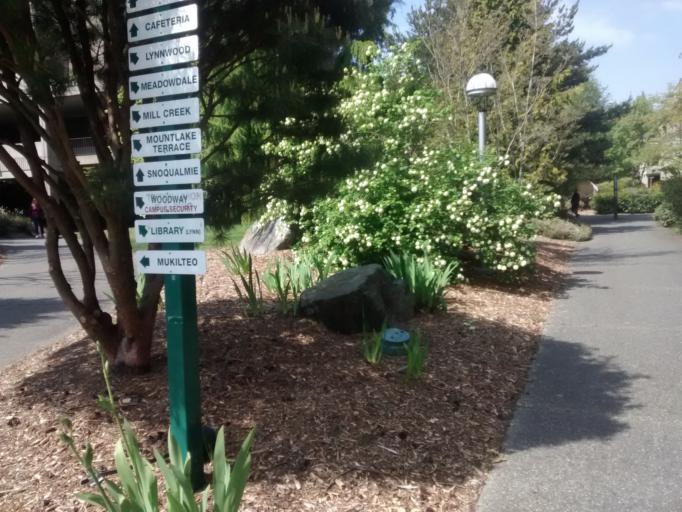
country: US
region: Washington
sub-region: Snohomish County
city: Lynnwood
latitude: 47.8151
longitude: -122.3272
